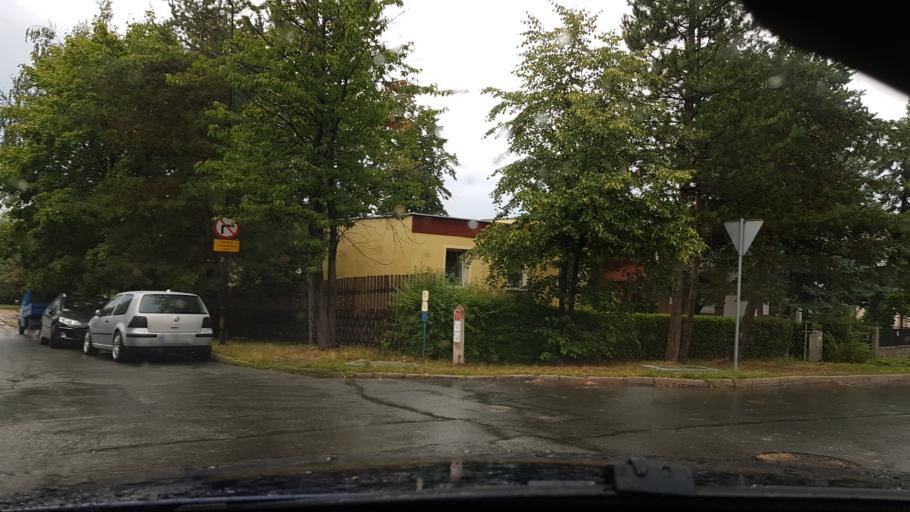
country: PL
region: Lower Silesian Voivodeship
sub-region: Jelenia Gora
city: Jelenia Gora
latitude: 50.8856
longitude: 15.7342
